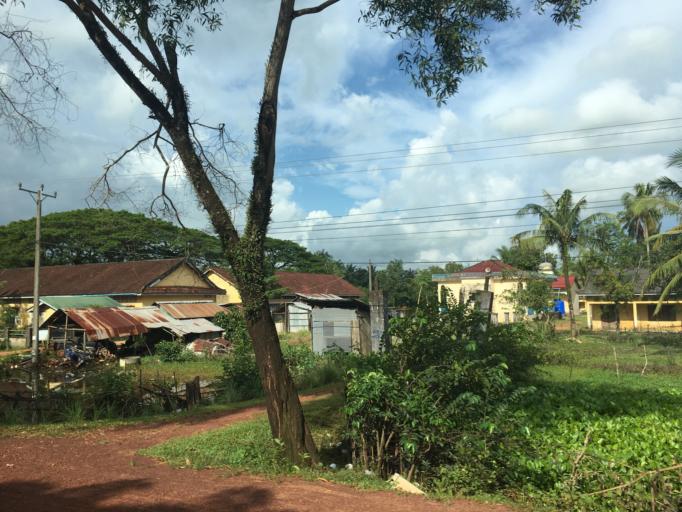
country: KH
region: Preah Sihanouk
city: Sihanoukville
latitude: 10.6437
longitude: 103.7869
